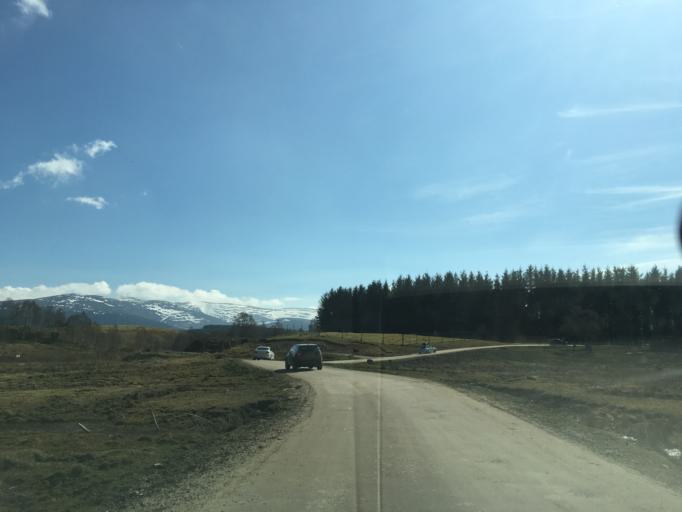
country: GB
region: Scotland
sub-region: Highland
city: Kingussie
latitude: 57.1118
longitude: -3.9718
